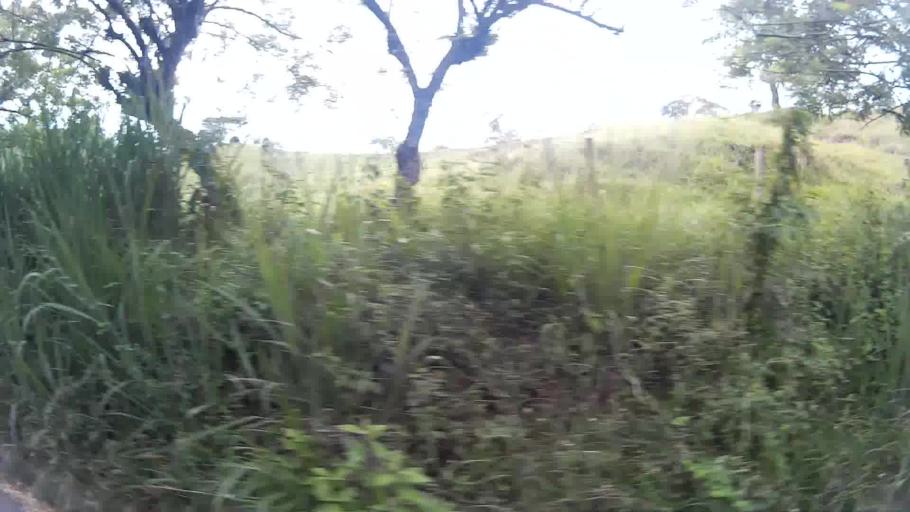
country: CO
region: Risaralda
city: La Virginia
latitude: 4.9349
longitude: -75.8513
